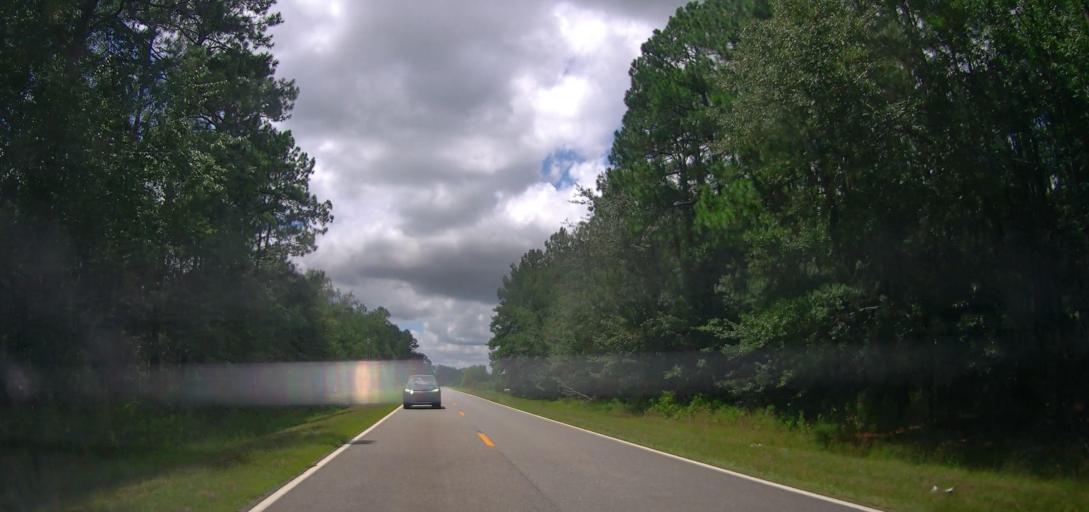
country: US
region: Georgia
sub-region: Irwin County
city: Ocilla
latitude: 31.6455
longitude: -83.3177
